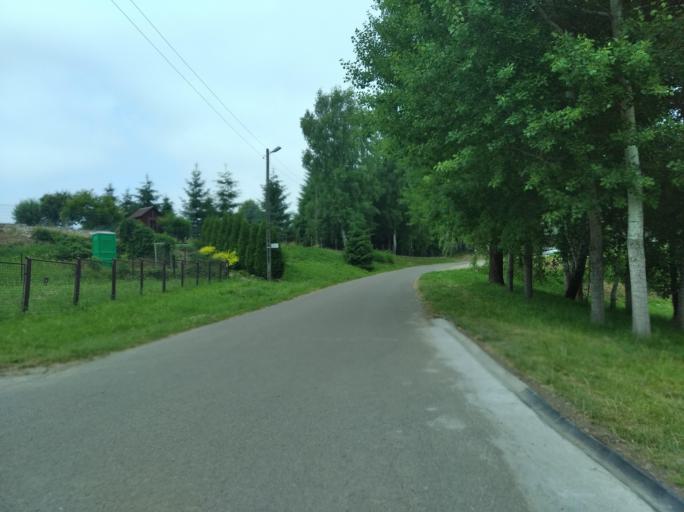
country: PL
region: Subcarpathian Voivodeship
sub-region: Powiat brzozowski
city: Haczow
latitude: 49.6695
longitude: 21.8911
